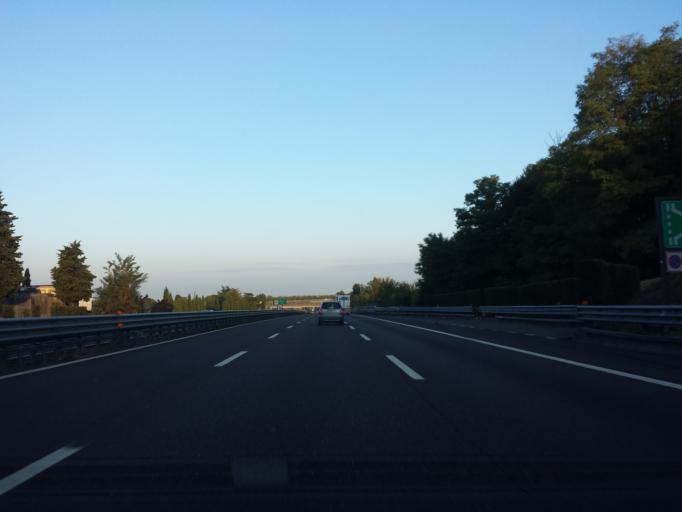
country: IT
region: Lombardy
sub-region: Provincia di Brescia
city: Calcinato
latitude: 45.4644
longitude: 10.4163
